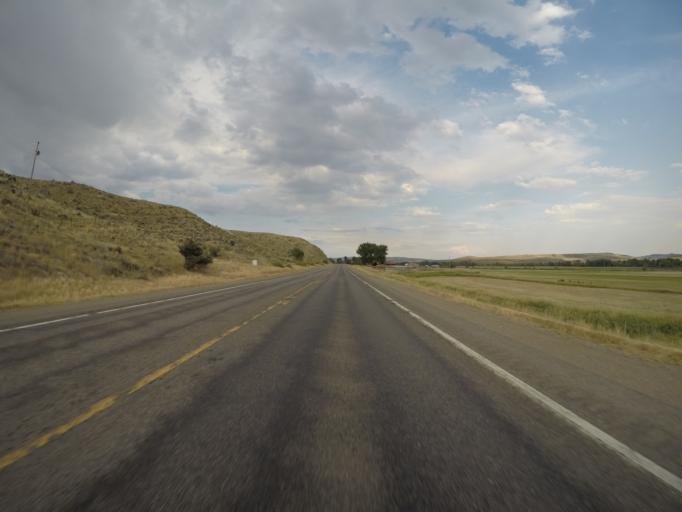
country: US
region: Colorado
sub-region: Moffat County
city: Craig
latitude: 40.5189
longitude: -107.4810
